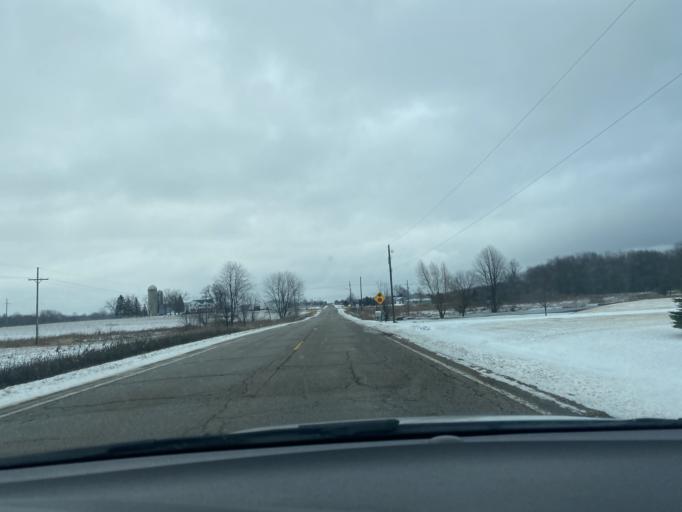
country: US
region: Michigan
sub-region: Lapeer County
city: North Branch
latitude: 43.2081
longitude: -83.1790
